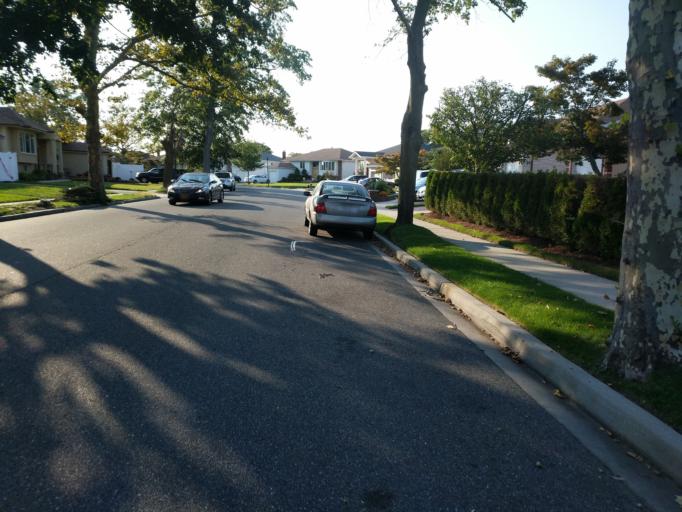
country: US
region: New York
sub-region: Nassau County
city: South Valley Stream
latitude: 40.6511
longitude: -73.7249
